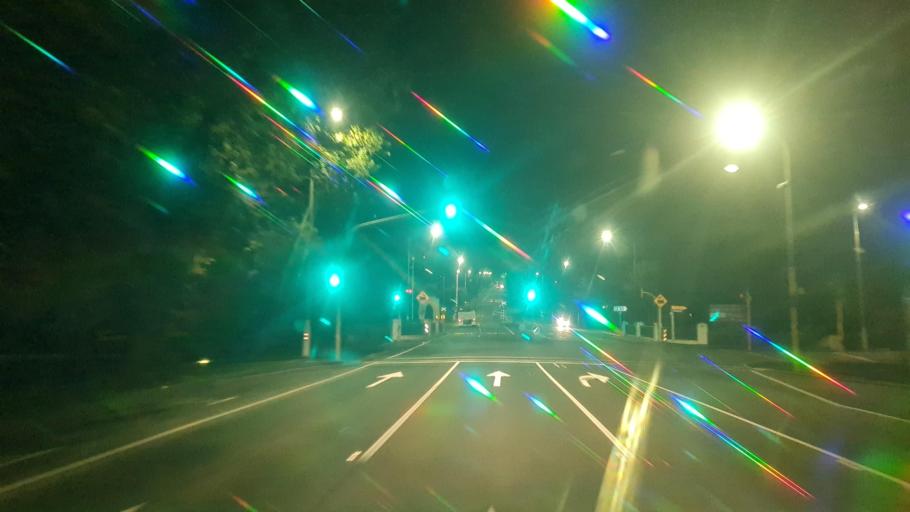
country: NZ
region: Otago
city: Oamaru
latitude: -45.0990
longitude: 170.9667
